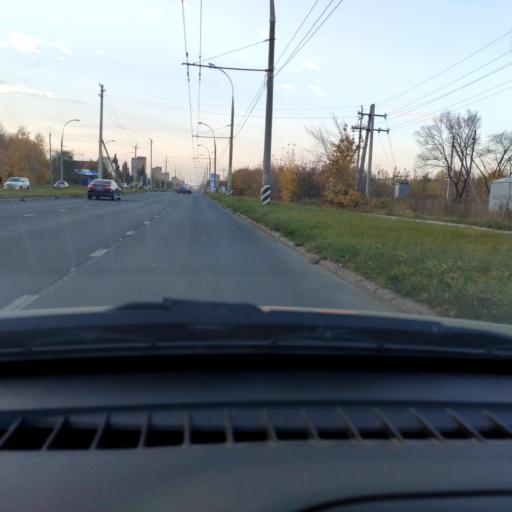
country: RU
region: Samara
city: Tol'yatti
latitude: 53.5423
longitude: 49.3005
